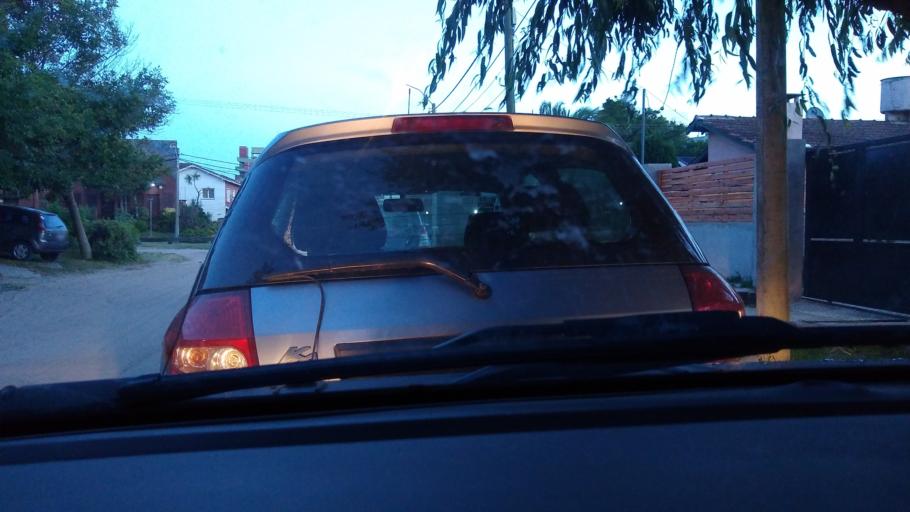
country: AR
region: Buenos Aires
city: Villa Gesell
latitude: -37.2754
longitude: -56.9832
